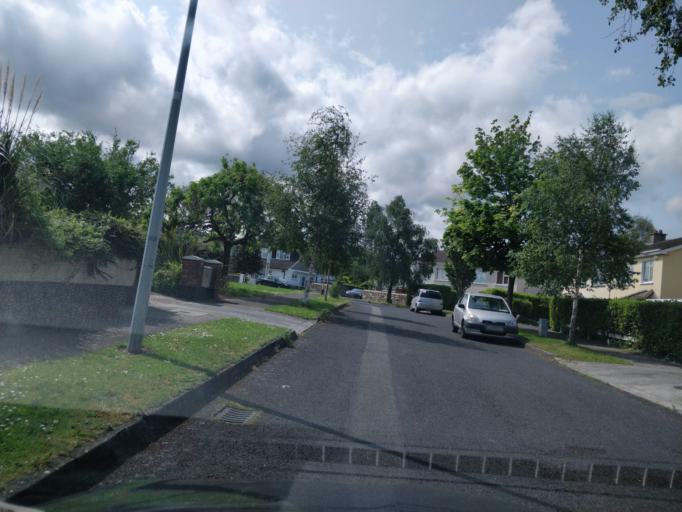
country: IE
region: Leinster
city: Dundrum
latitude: 53.2860
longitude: -6.2655
